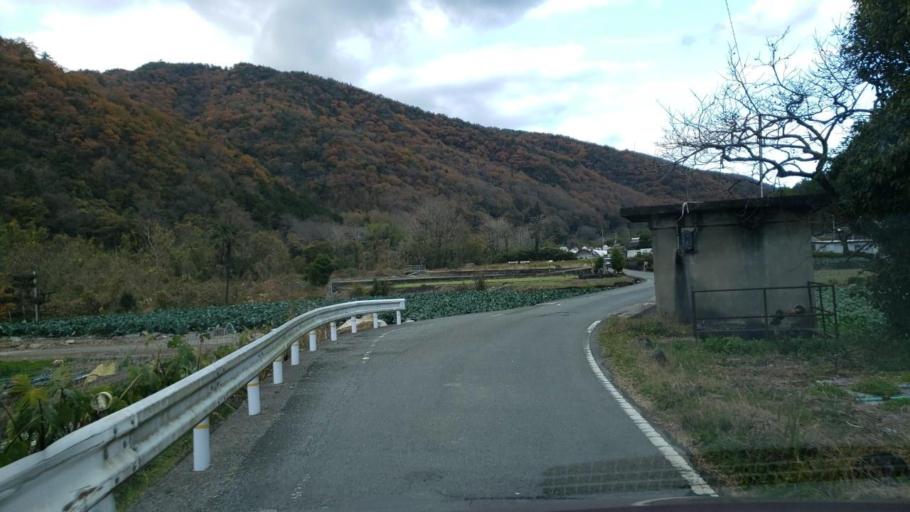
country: JP
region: Tokushima
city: Wakimachi
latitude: 34.1056
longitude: 134.2243
